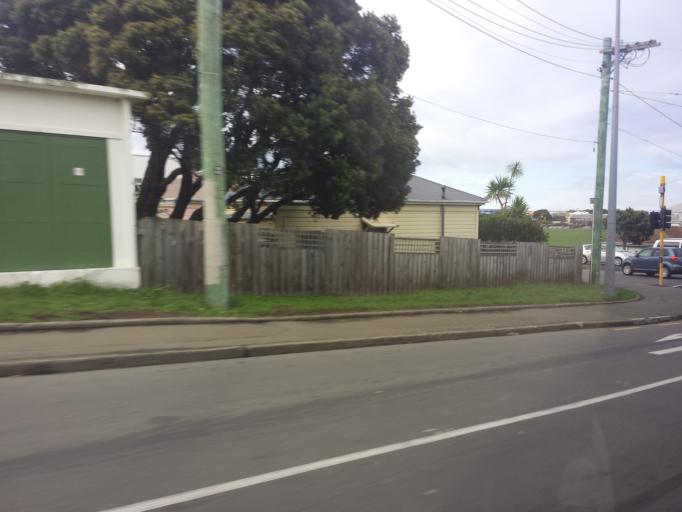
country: NZ
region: Wellington
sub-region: Wellington City
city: Wellington
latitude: -41.3118
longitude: 174.7936
